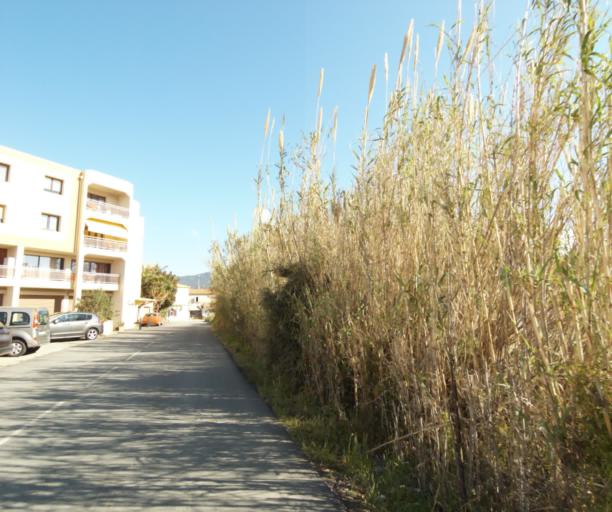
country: FR
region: Corsica
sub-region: Departement de la Corse-du-Sud
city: Propriano
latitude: 41.6745
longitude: 8.8989
